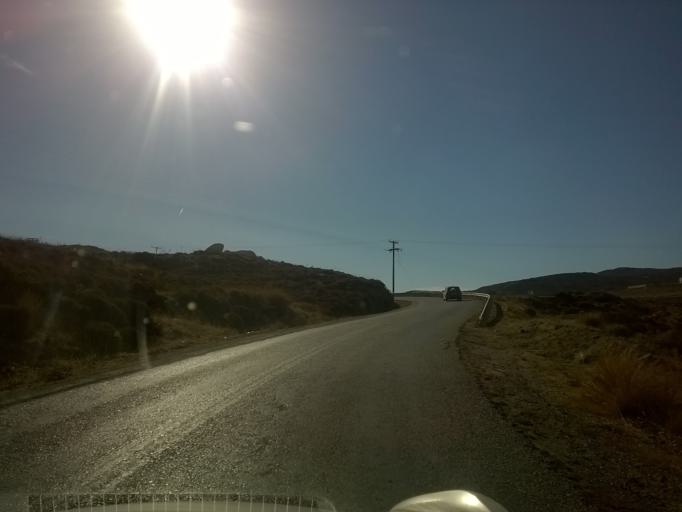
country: GR
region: South Aegean
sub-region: Nomos Kykladon
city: Naxos
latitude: 37.1203
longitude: 25.4147
